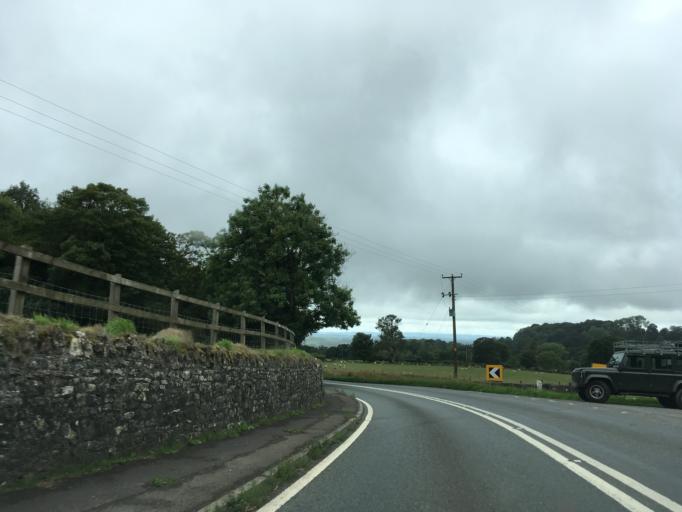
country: GB
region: England
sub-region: Somerset
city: Wells
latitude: 51.2213
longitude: -2.6370
